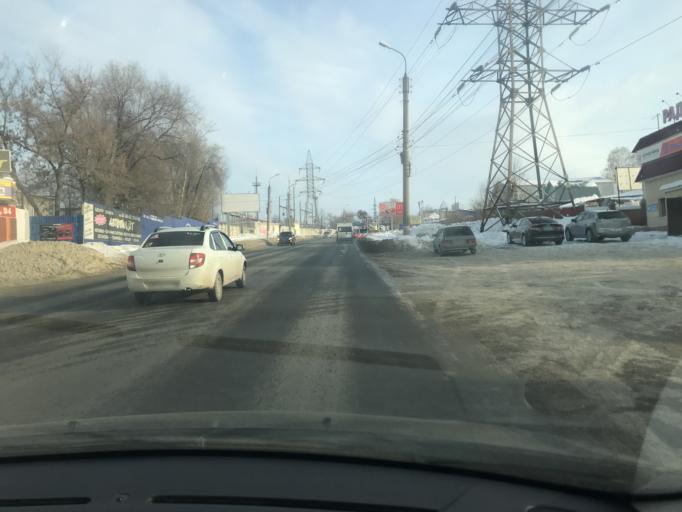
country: RU
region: Ulyanovsk
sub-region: Ulyanovskiy Rayon
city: Ulyanovsk
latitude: 54.3307
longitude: 48.3632
